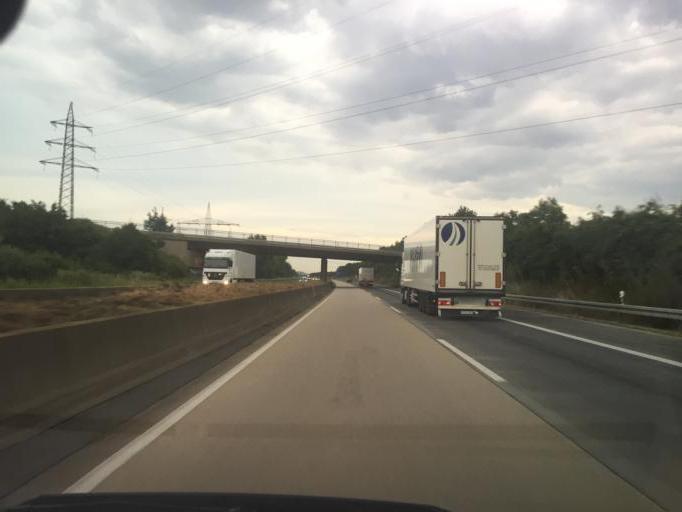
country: DE
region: North Rhine-Westphalia
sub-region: Regierungsbezirk Koln
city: Elsdorf
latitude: 50.9526
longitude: 6.5889
